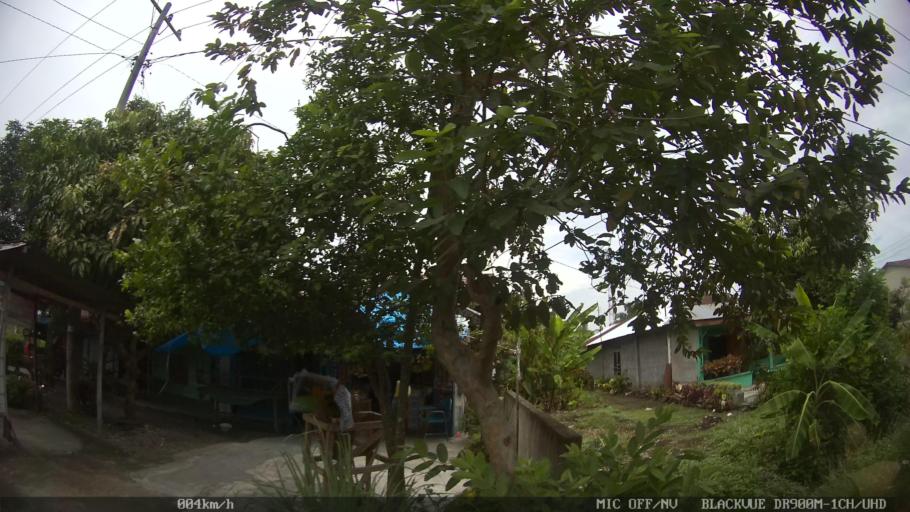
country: ID
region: North Sumatra
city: Sunggal
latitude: 3.6069
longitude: 98.5543
